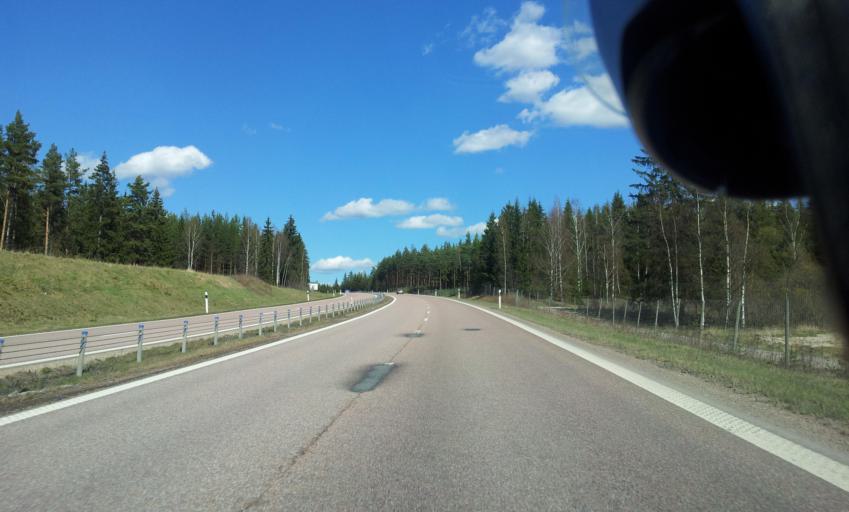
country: SE
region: Dalarna
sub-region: Borlange Kommun
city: Ornas
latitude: 60.5178
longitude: 15.5496
